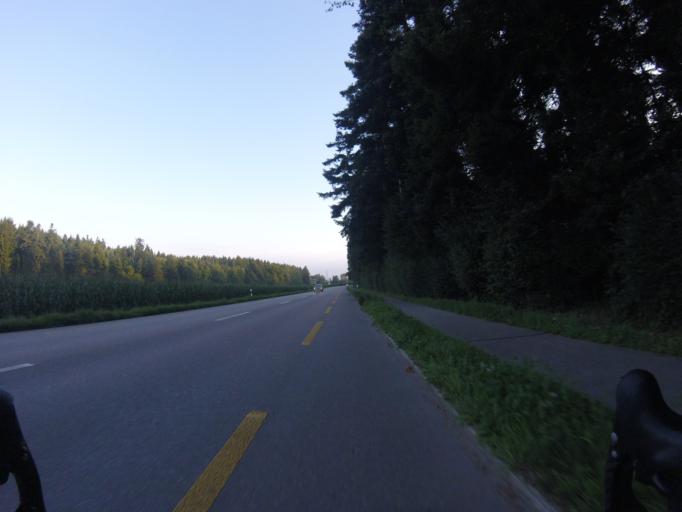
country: CH
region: Bern
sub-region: Thun District
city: Heimberg
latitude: 46.8051
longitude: 7.5955
